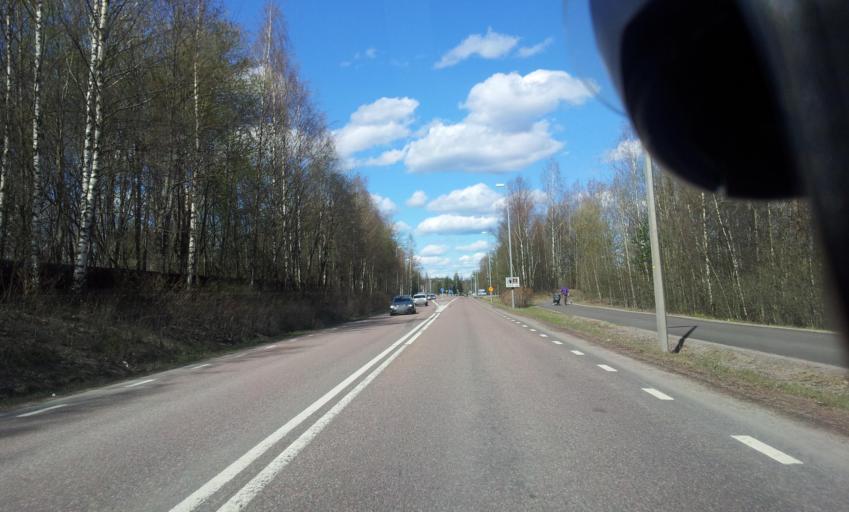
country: SE
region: Dalarna
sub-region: Faluns Kommun
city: Falun
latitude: 60.6140
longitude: 15.6150
